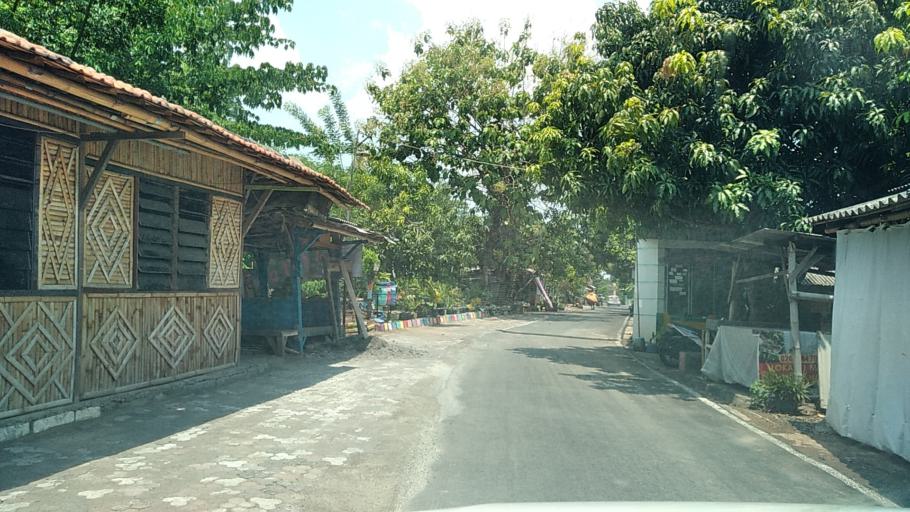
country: ID
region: Central Java
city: Semarang
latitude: -7.0051
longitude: 110.4414
